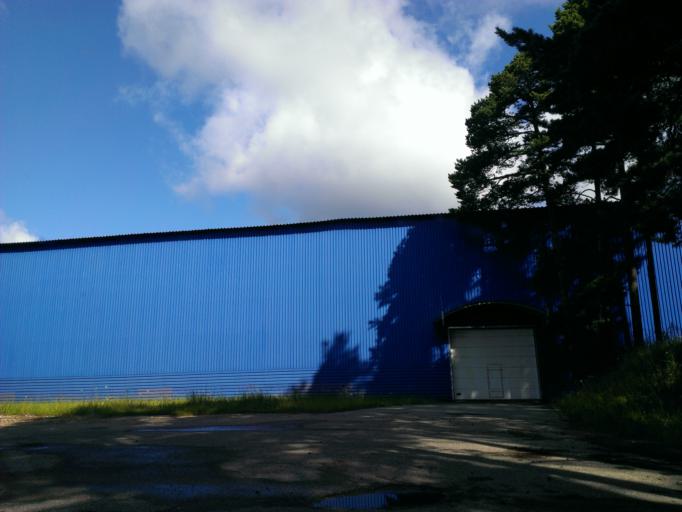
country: LV
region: Incukalns
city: Vangazi
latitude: 57.0862
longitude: 24.5156
